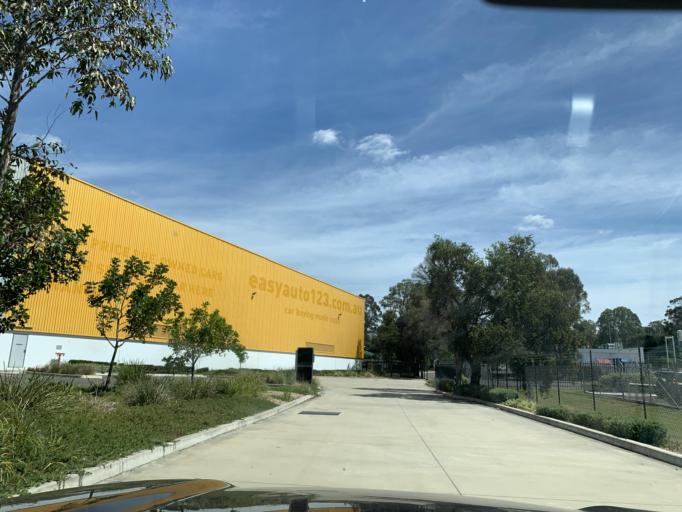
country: AU
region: New South Wales
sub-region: Holroyd
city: Girraween
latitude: -33.7682
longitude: 150.9521
